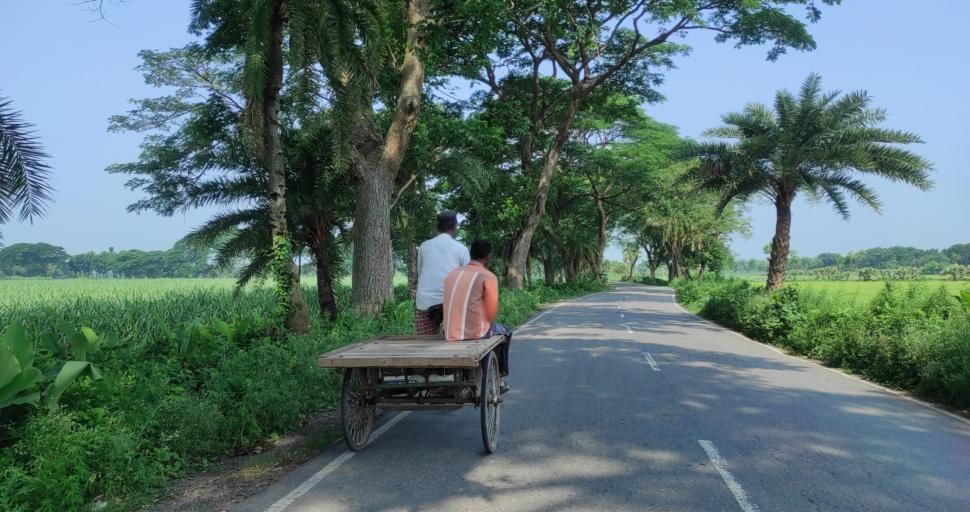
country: BD
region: Rajshahi
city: Ishurdi
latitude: 24.2785
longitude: 89.0612
